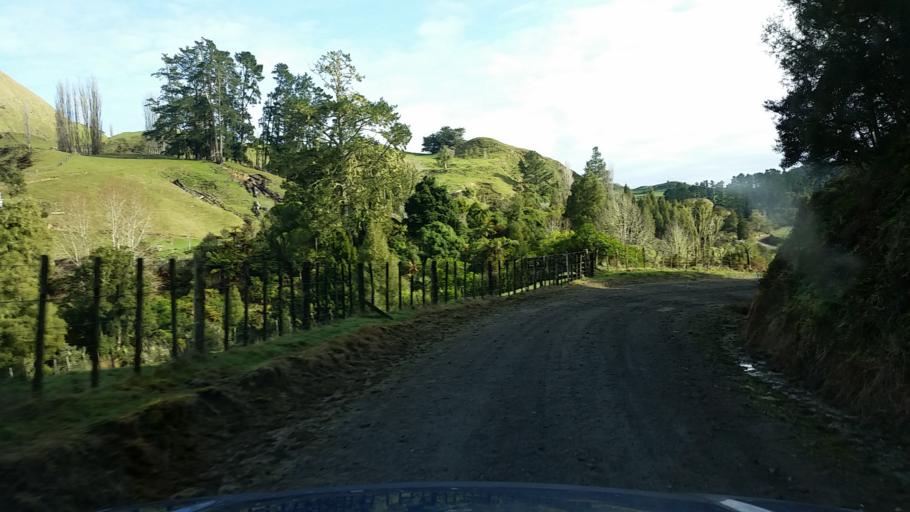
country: NZ
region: Taranaki
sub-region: New Plymouth District
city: Waitara
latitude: -39.1130
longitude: 174.8536
